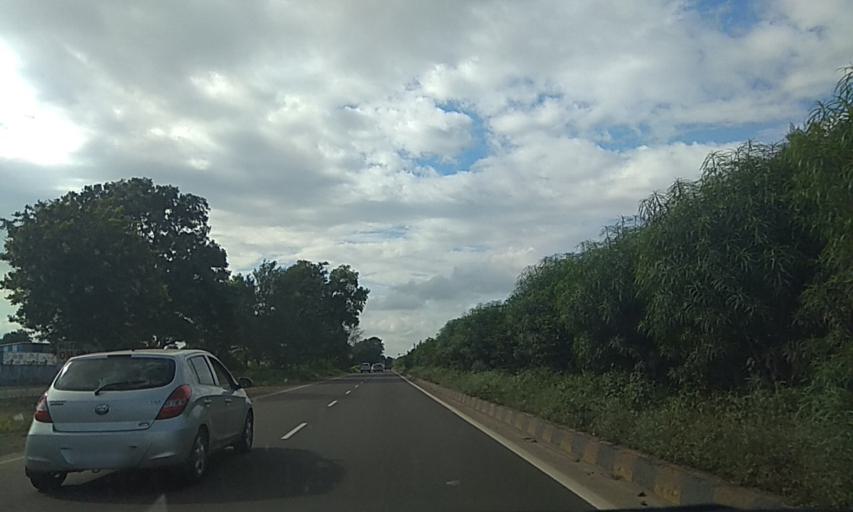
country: IN
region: Maharashtra
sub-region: Satara Division
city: Karad
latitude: 17.1177
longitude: 74.1966
